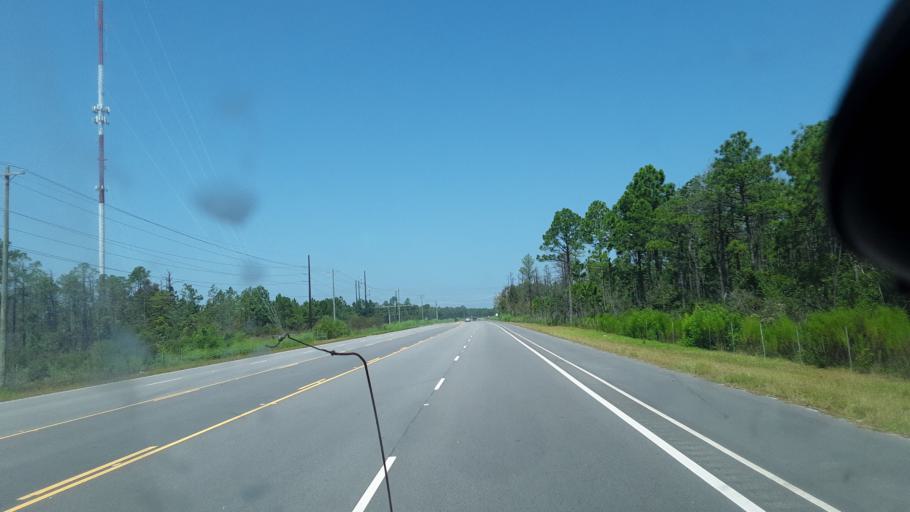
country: US
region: South Carolina
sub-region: Horry County
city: Myrtle Beach
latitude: 33.7829
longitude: -78.8759
